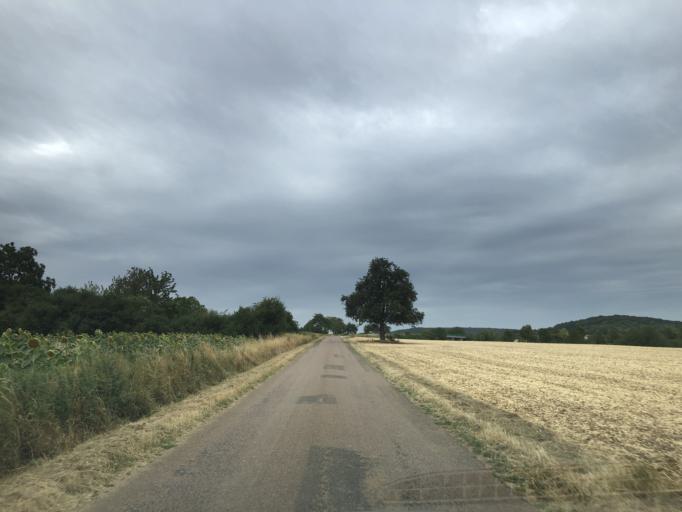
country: FR
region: Bourgogne
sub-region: Departement de l'Yonne
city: Aillant-sur-Tholon
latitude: 47.9097
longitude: 3.3434
